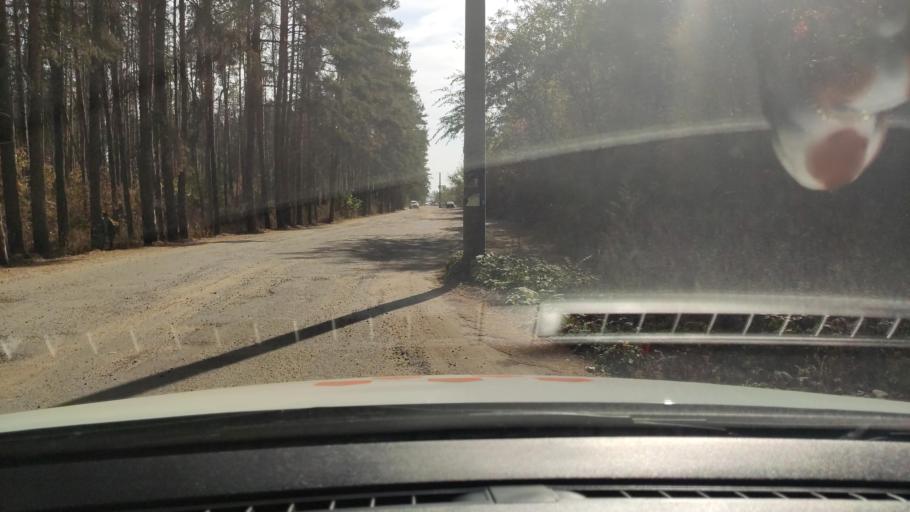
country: RU
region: Voronezj
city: Podgornoye
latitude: 51.7217
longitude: 39.1608
